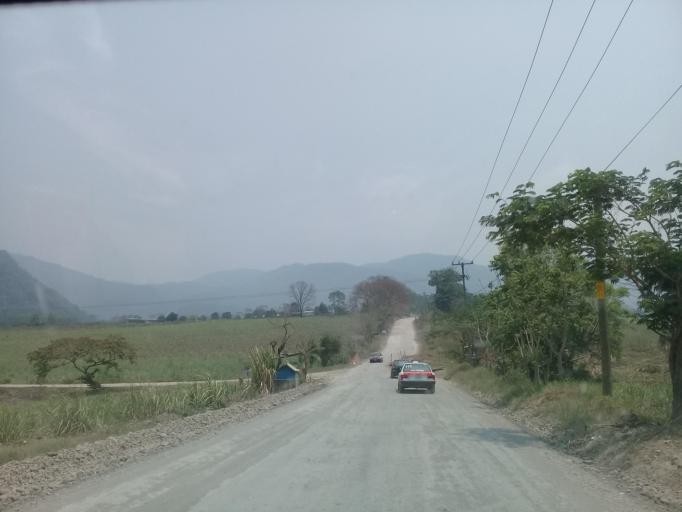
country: MX
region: Veracruz
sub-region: Tezonapa
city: Laguna Chica (Pueblo Nuevo)
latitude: 18.5676
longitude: -96.7202
